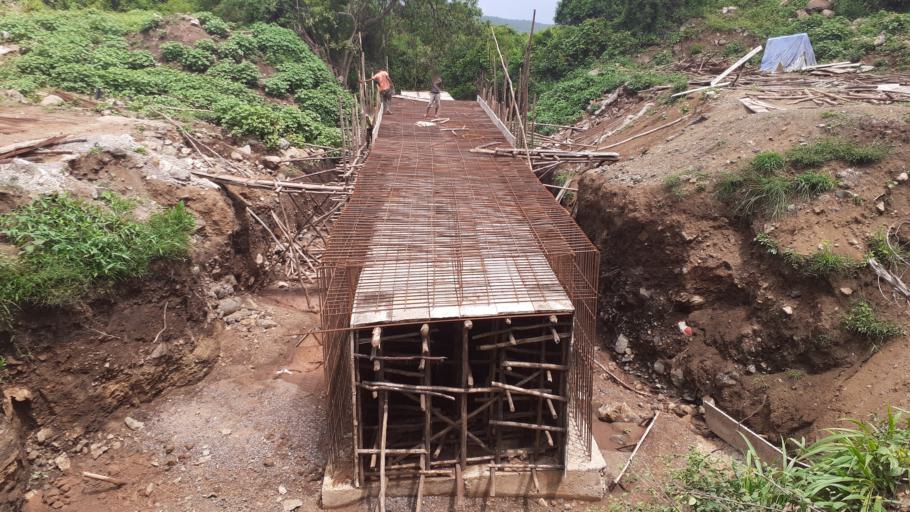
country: ET
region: Southern Nations, Nationalities, and People's Region
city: Areka
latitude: 7.5770
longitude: 37.5115
